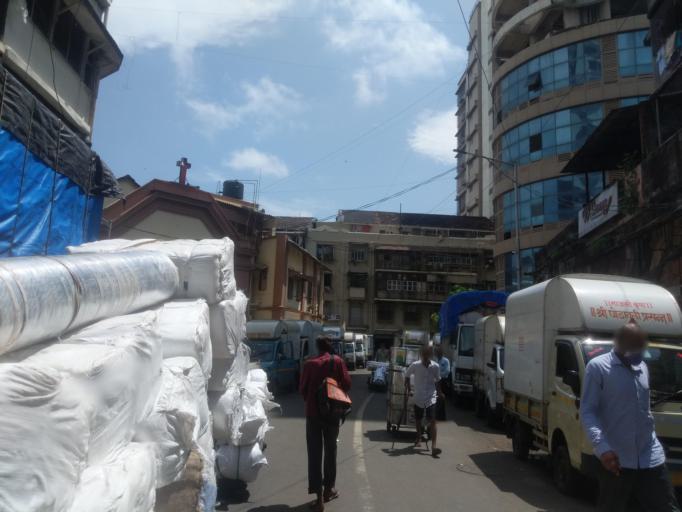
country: IN
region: Maharashtra
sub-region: Raigarh
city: Uran
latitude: 18.9494
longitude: 72.8274
